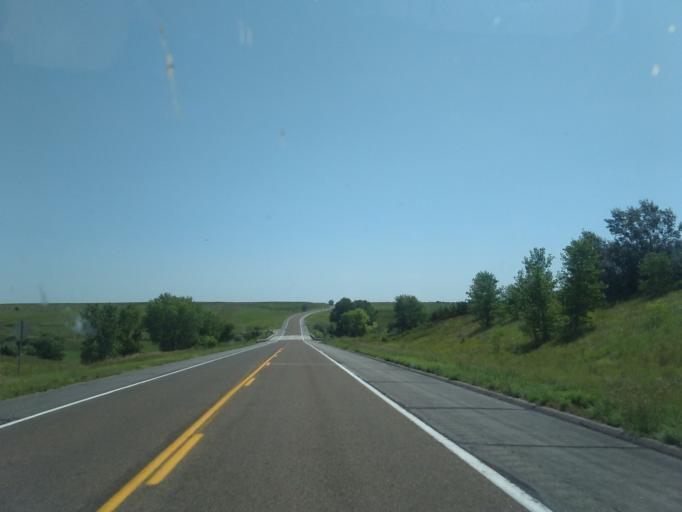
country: US
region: Nebraska
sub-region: Hitchcock County
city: Trenton
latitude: 40.1756
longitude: -101.1386
